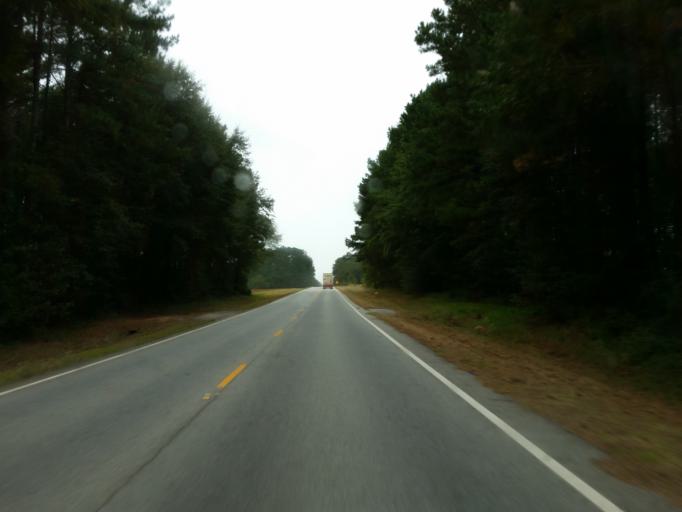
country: US
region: Georgia
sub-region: Berrien County
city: Ray City
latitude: 31.1064
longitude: -83.2856
